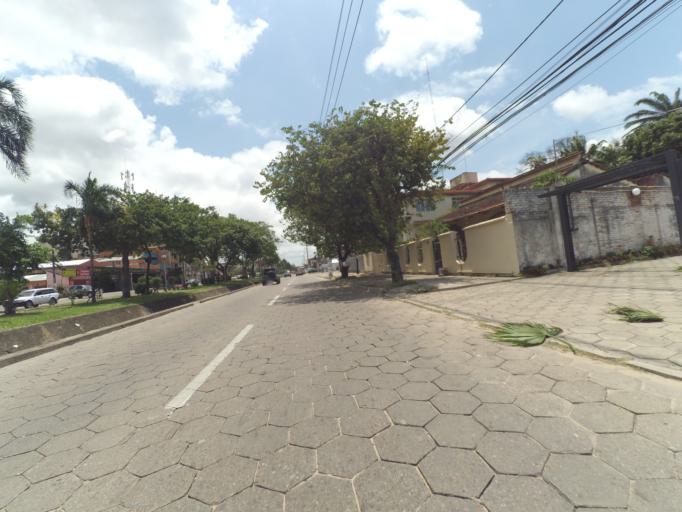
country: BO
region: Santa Cruz
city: Santa Cruz de la Sierra
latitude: -17.7852
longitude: -63.1988
